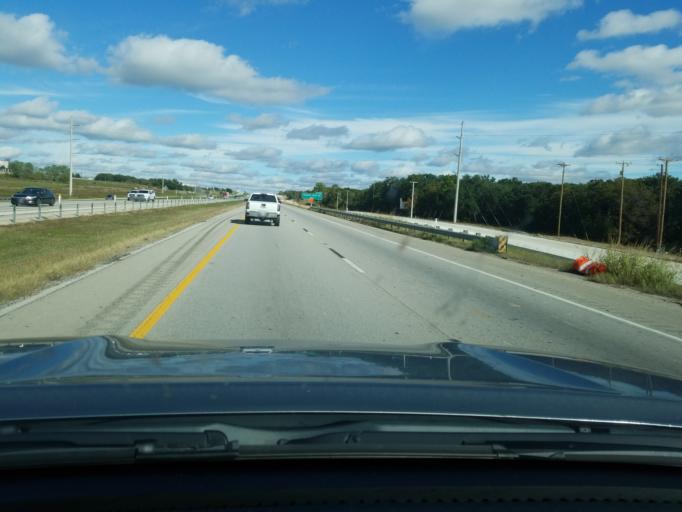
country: US
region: Texas
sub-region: Parker County
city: Hudson Oaks
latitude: 32.7501
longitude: -97.7216
